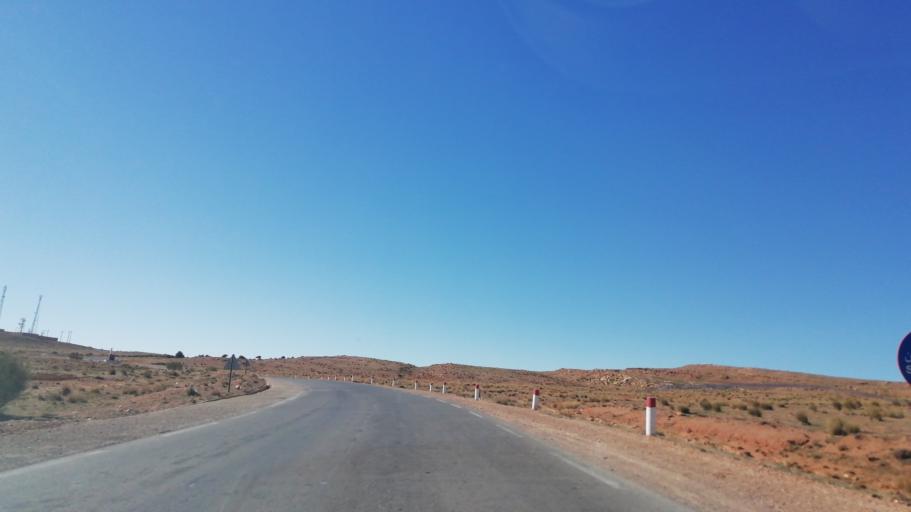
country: DZ
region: El Bayadh
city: El Bayadh
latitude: 33.6652
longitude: 1.4303
